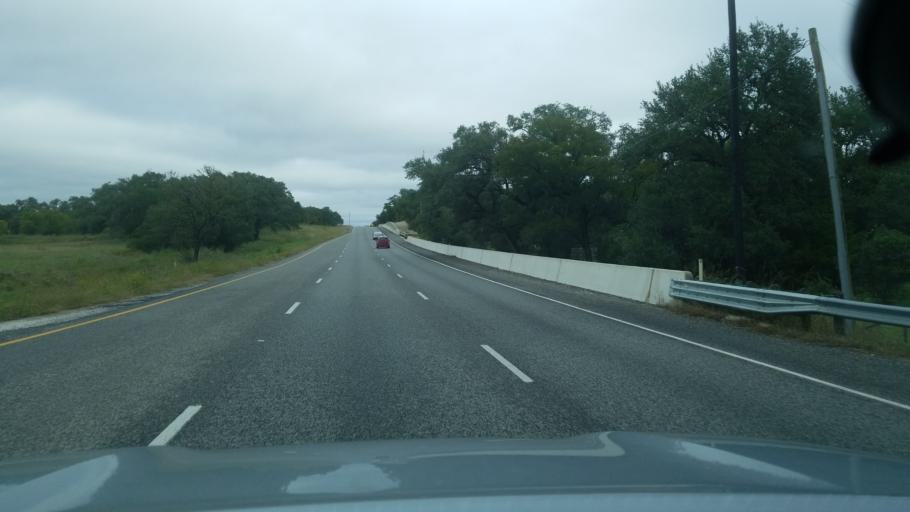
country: US
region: Texas
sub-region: Comal County
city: Canyon Lake
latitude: 29.8972
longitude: -98.4102
